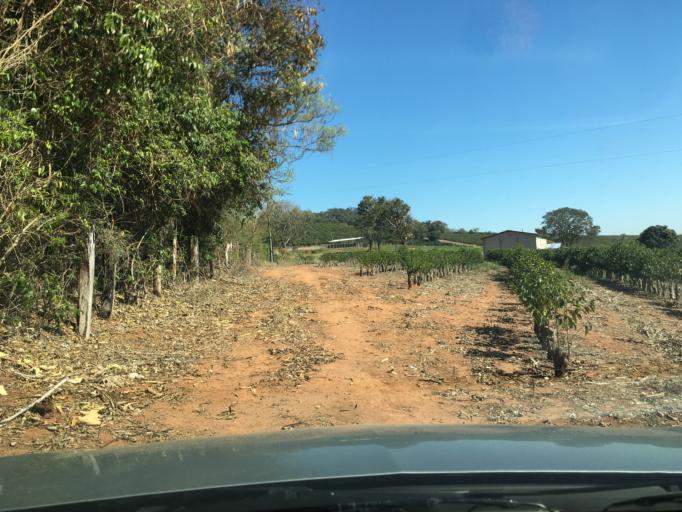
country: BR
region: Minas Gerais
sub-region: Campestre
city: Campestre
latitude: -21.5924
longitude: -46.2057
